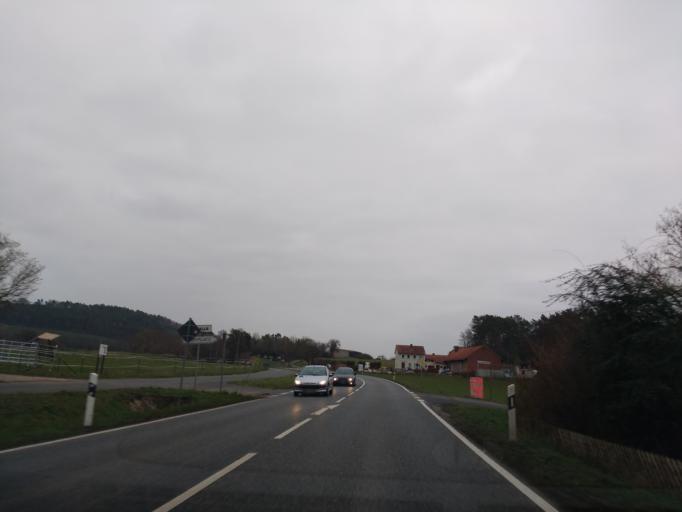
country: DE
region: Hesse
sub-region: Regierungsbezirk Kassel
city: Alheim
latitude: 51.0614
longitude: 9.6260
